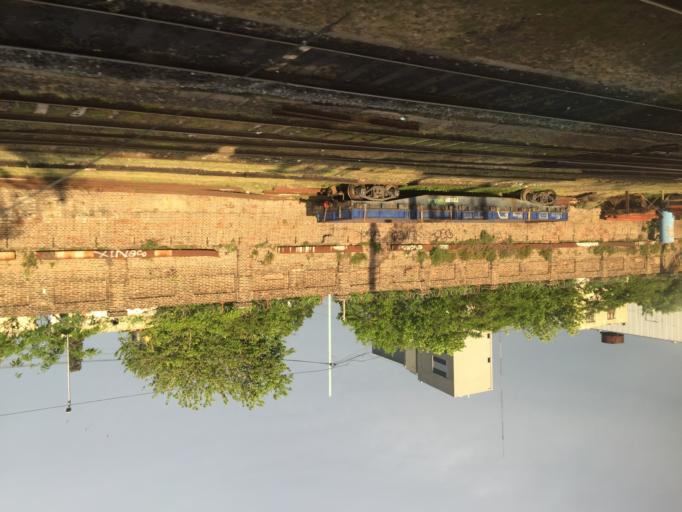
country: AR
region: Buenos Aires F.D.
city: Buenos Aires
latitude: -34.6348
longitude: -58.3805
